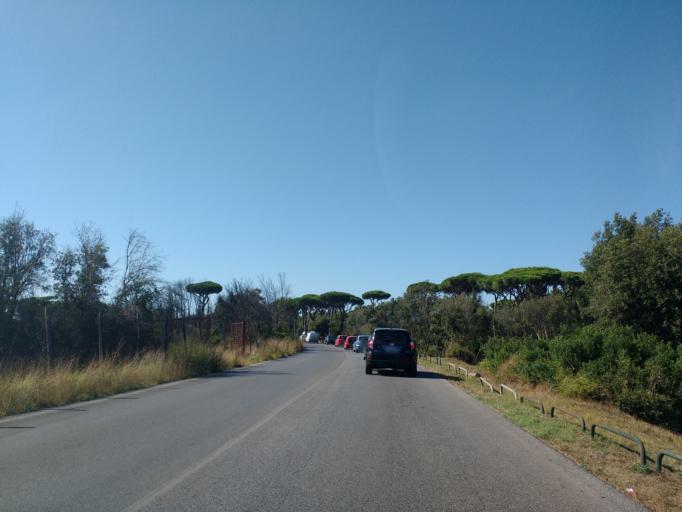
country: IT
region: Latium
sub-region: Citta metropolitana di Roma Capitale
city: Acilia-Castel Fusano-Ostia Antica
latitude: 41.7287
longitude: 12.3387
